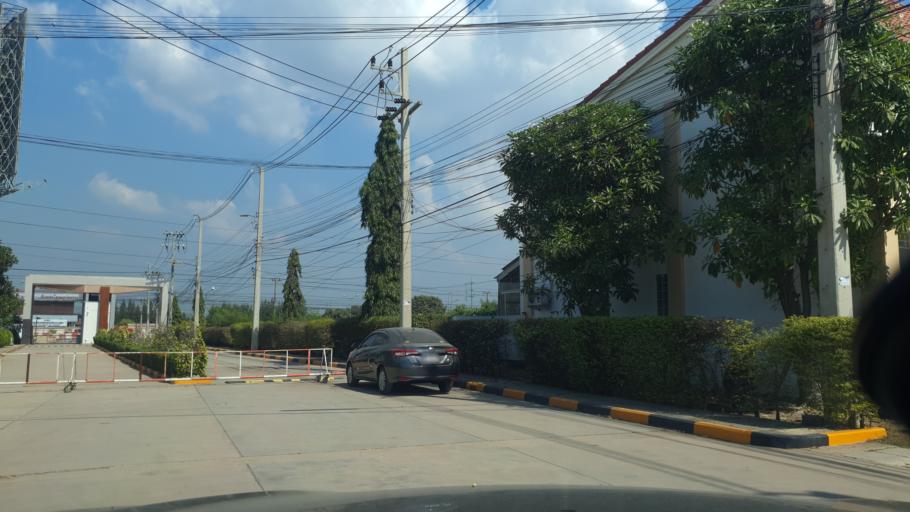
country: TH
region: Samut Sakhon
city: Samut Sakhon
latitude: 13.5291
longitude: 100.2019
